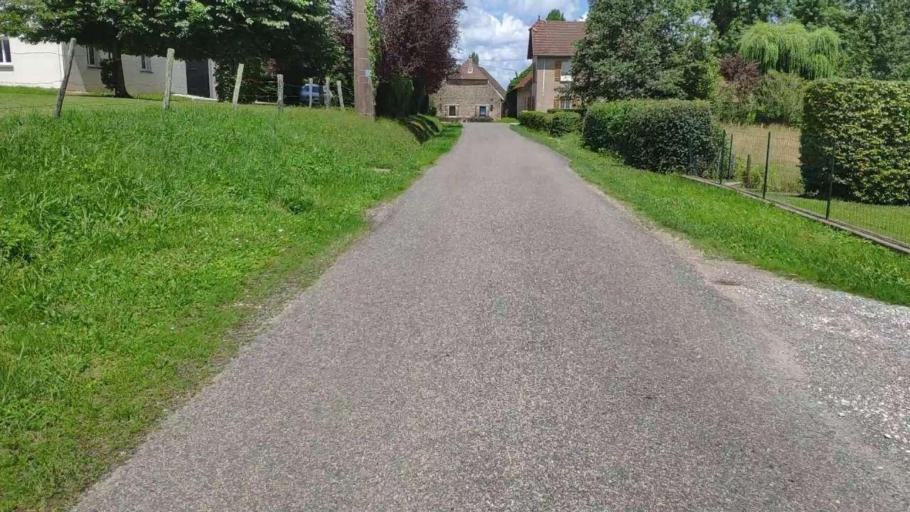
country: FR
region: Franche-Comte
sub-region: Departement du Jura
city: Bletterans
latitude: 46.8458
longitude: 5.4726
